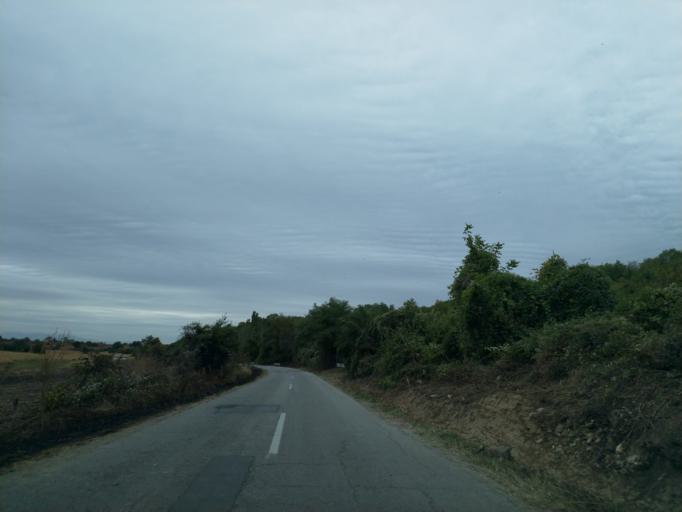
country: RS
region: Central Serbia
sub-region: Pomoravski Okrug
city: Paracin
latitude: 43.8496
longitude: 21.3224
